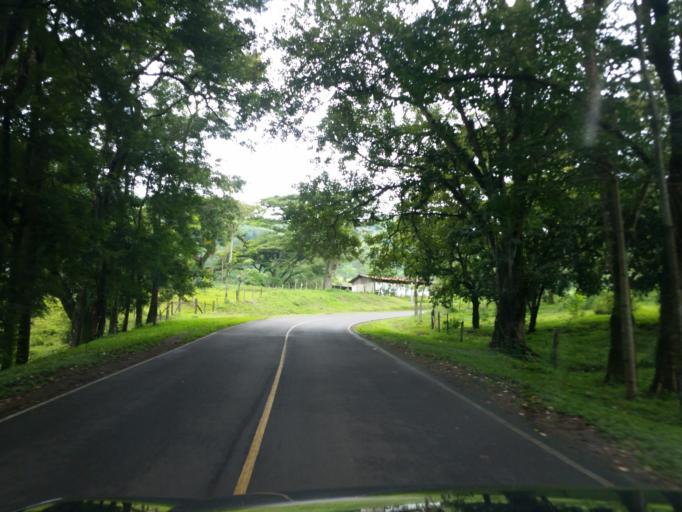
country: NI
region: Matagalpa
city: San Ramon
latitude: 13.0442
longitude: -85.7683
